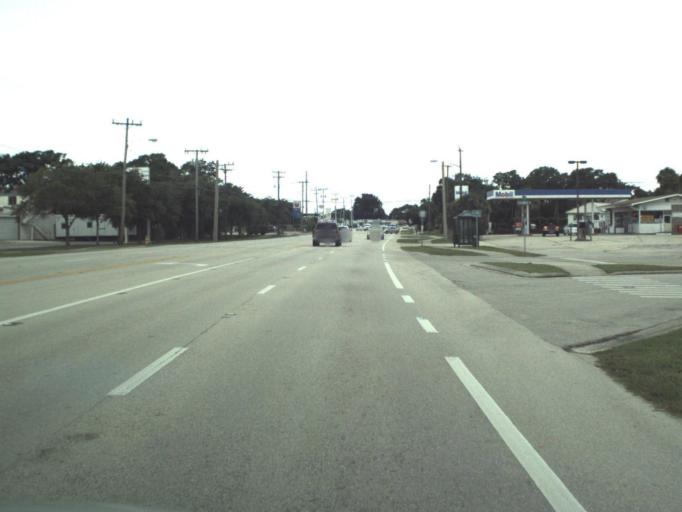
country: US
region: Florida
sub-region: Brevard County
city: Cape Canaveral
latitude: 28.3913
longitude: -80.6080
